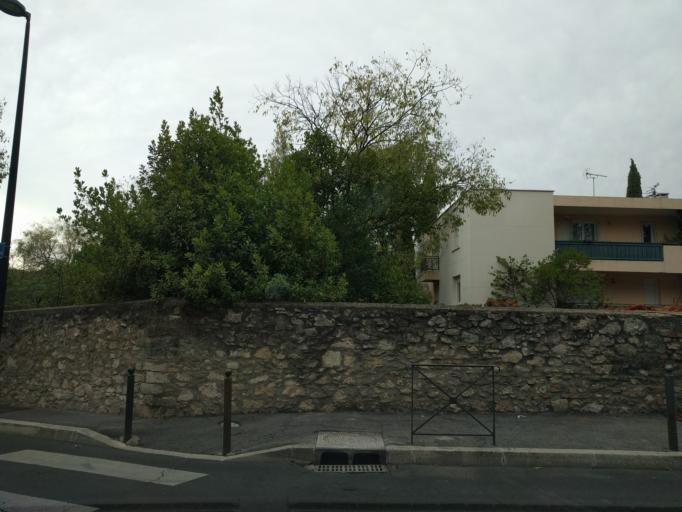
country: FR
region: Languedoc-Roussillon
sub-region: Departement de l'Herault
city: Montpellier
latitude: 43.6309
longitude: 3.8729
